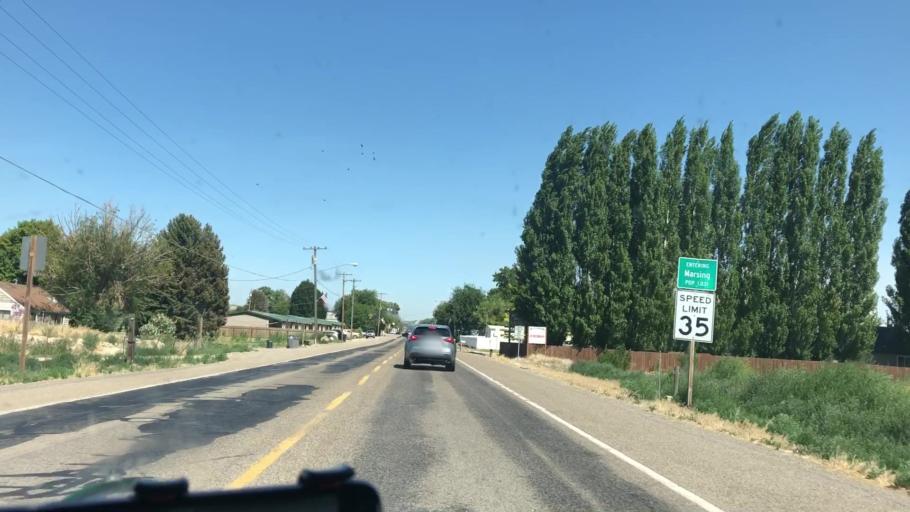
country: US
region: Idaho
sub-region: Owyhee County
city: Marsing
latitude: 43.5453
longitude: -116.8200
